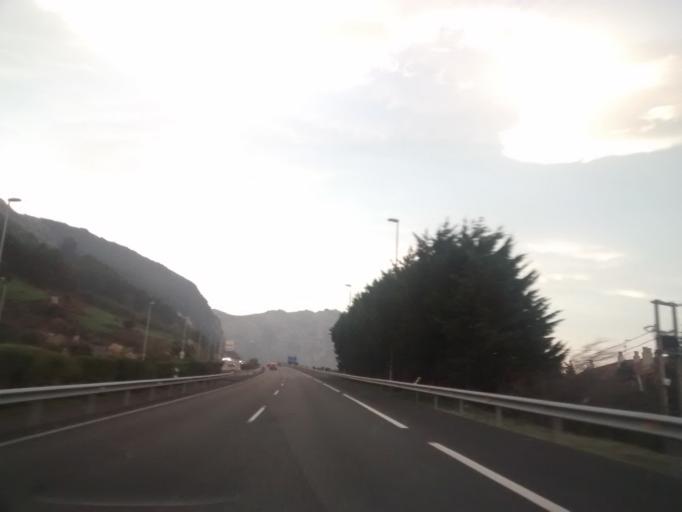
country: ES
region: Cantabria
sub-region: Provincia de Cantabria
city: Castro-Urdiales
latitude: 43.4025
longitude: -3.2925
